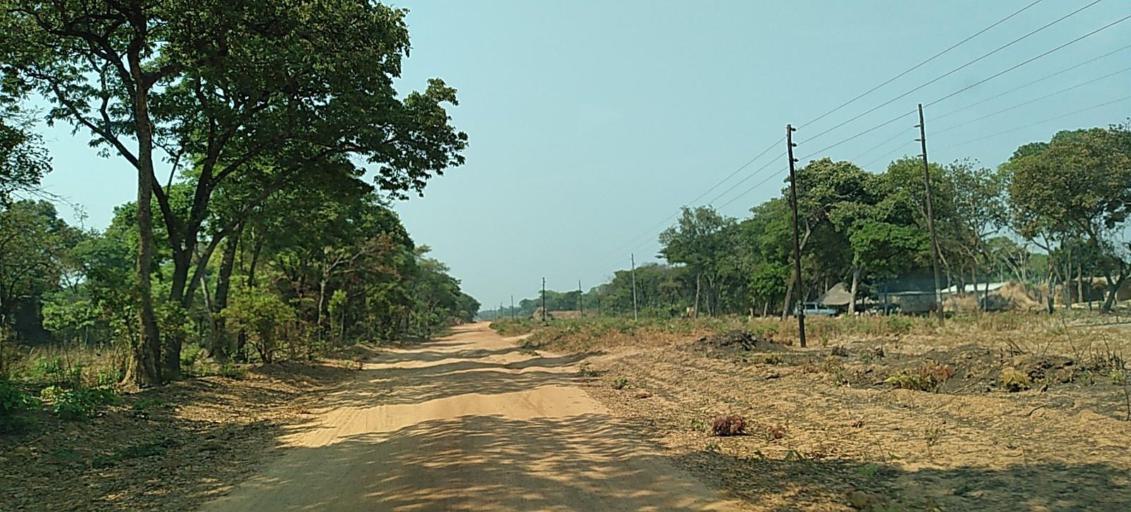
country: ZM
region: Copperbelt
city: Kalulushi
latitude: -13.0936
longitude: 27.4067
